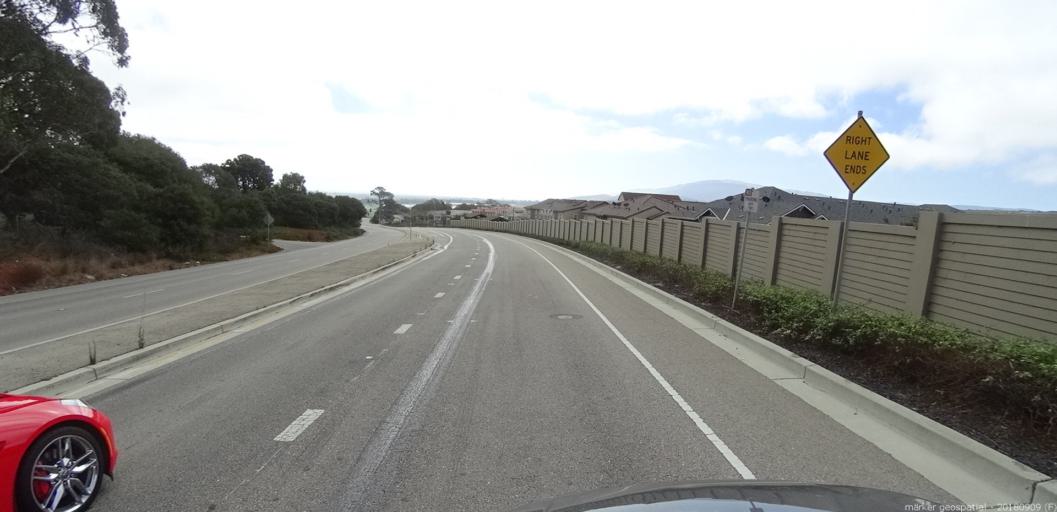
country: US
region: California
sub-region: Monterey County
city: Marina
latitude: 36.6564
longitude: -121.7350
